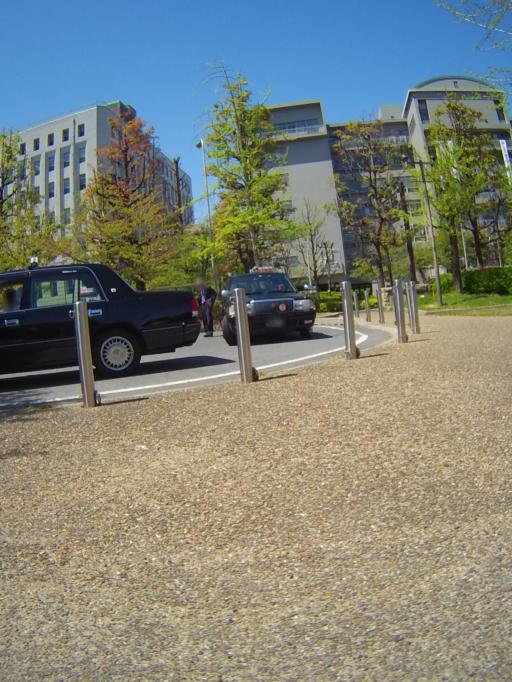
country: JP
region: Osaka
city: Osaka-shi
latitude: 34.6872
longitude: 135.5207
